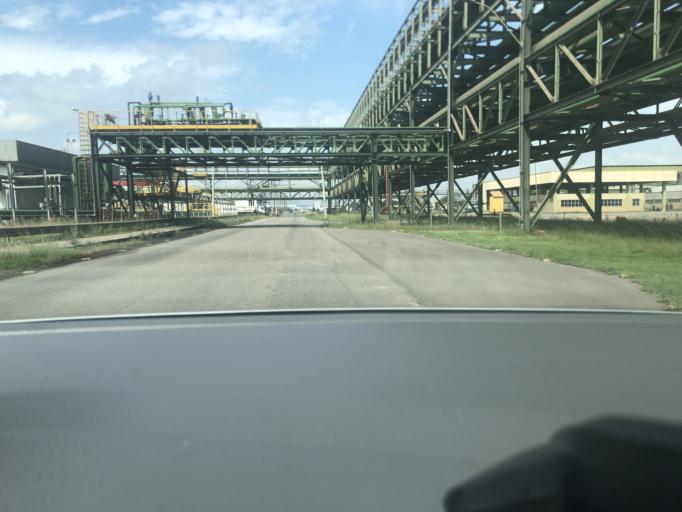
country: BR
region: Rio de Janeiro
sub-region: Itaguai
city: Itaguai
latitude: -22.9048
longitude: -43.7384
